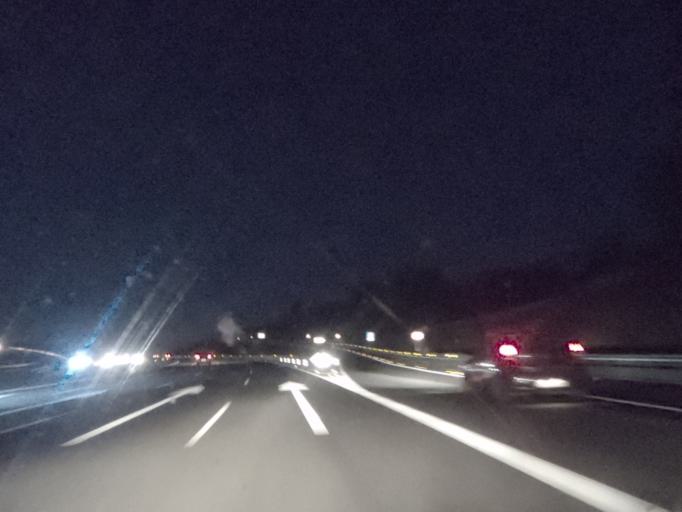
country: ES
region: Galicia
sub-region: Provincia da Coruna
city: Santiago de Compostela
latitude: 42.8652
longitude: -8.5192
